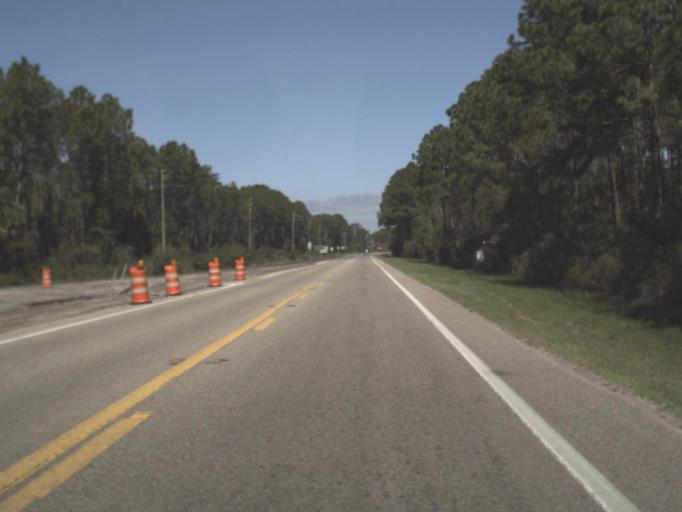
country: US
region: Florida
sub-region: Gulf County
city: Port Saint Joe
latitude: 29.7806
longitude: -85.2998
